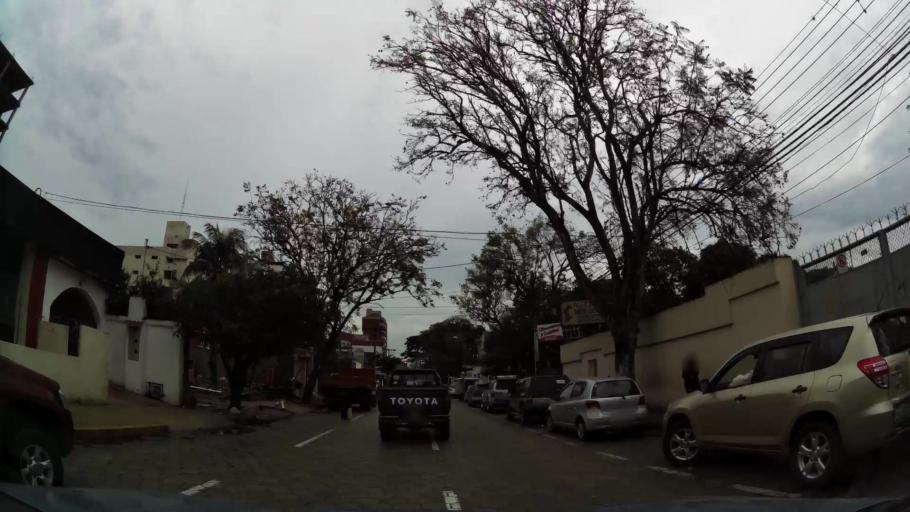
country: BO
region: Santa Cruz
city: Santa Cruz de la Sierra
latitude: -17.7932
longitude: -63.1804
